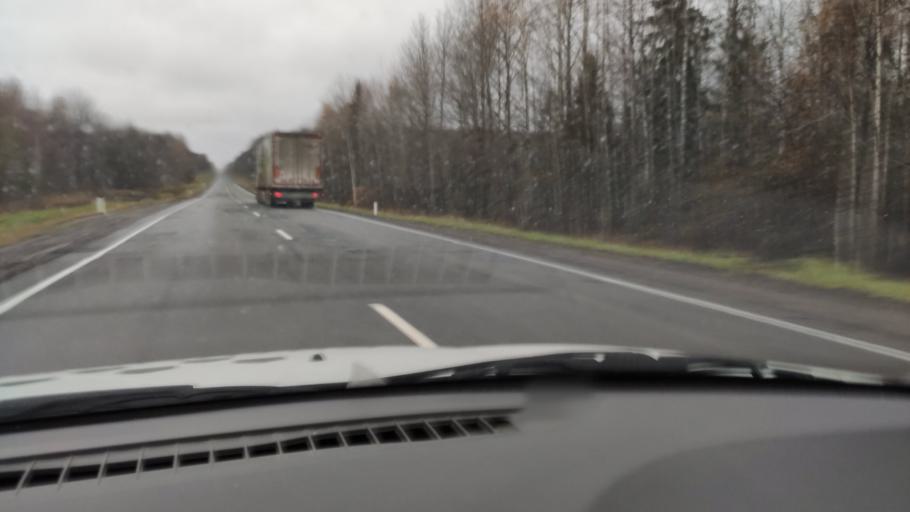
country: RU
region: Kirov
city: Omutninsk
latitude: 58.7550
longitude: 52.0406
